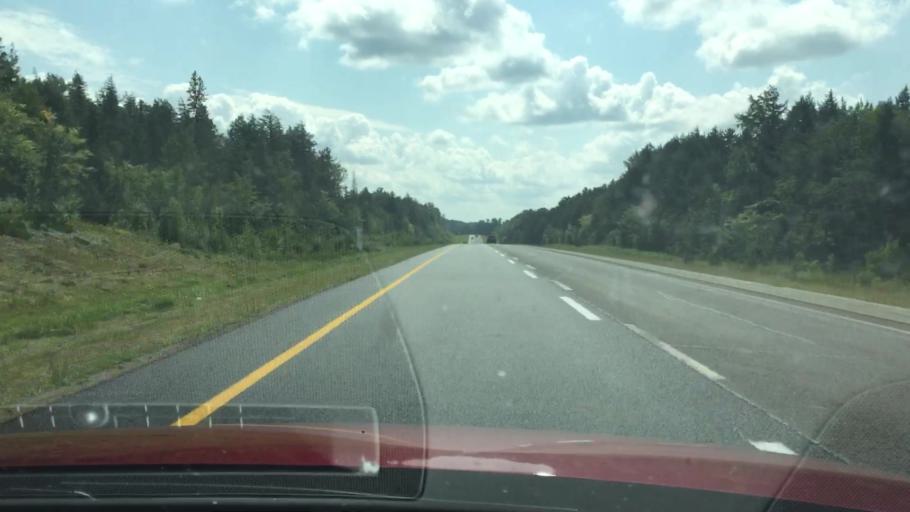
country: US
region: Maine
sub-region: Penobscot County
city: Medway
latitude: 45.7298
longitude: -68.4728
